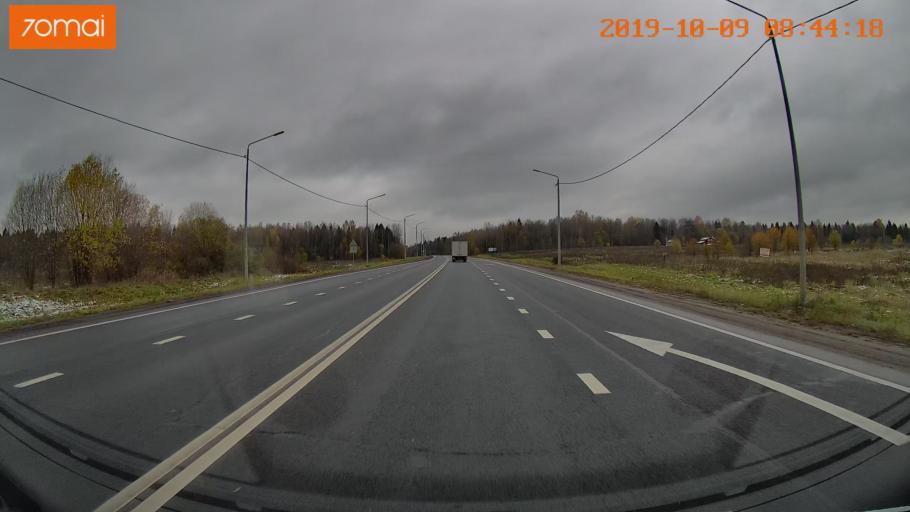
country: RU
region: Vologda
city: Gryazovets
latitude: 59.0348
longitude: 40.1089
